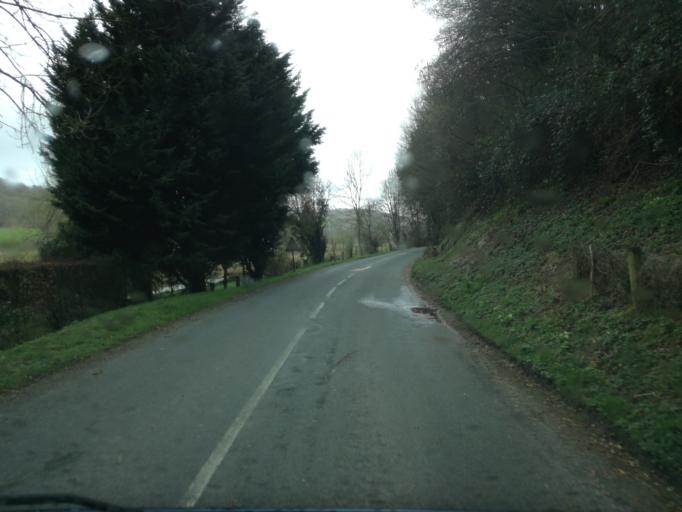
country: FR
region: Haute-Normandie
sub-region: Departement de la Seine-Maritime
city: Saint-Wandrille-Rancon
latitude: 49.5351
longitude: 0.7549
